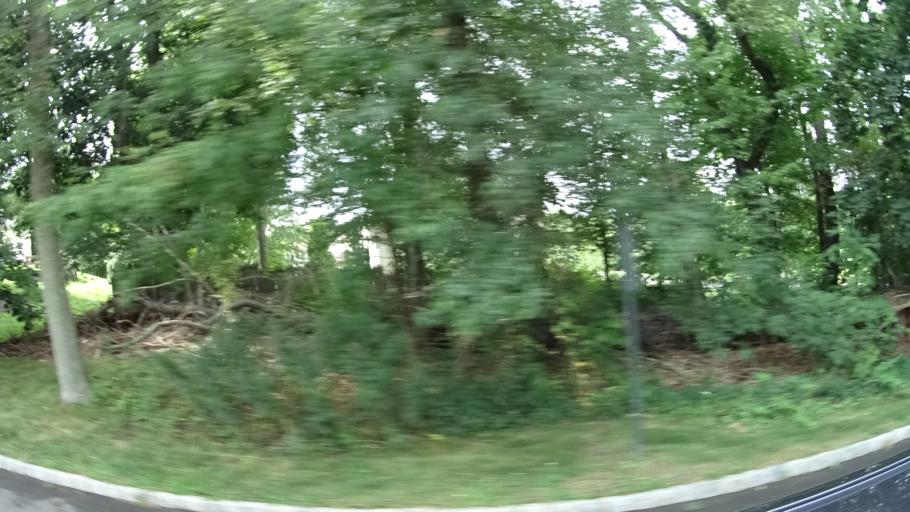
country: US
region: New Jersey
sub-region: Union County
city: Berkeley Heights
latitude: 40.6780
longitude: -74.4560
